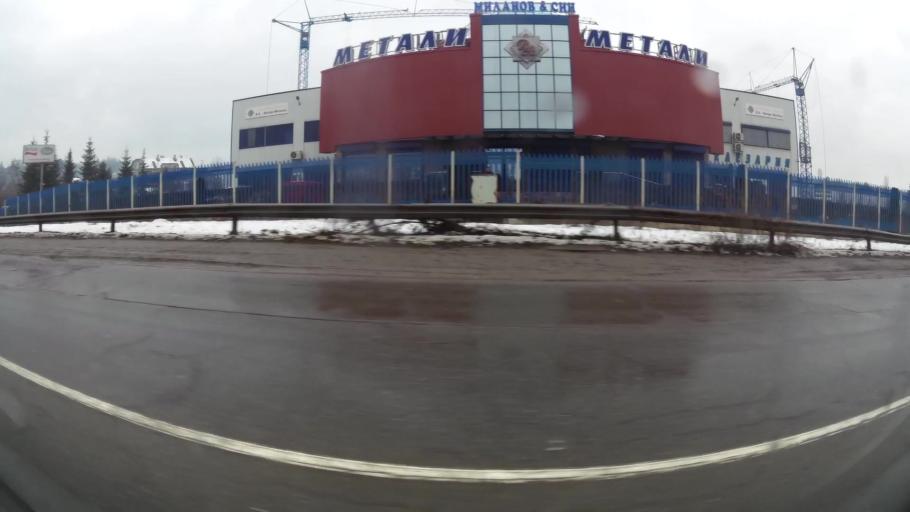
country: BG
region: Sofiya
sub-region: Obshtina Bozhurishte
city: Bozhurishte
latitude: 42.6899
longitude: 23.2304
